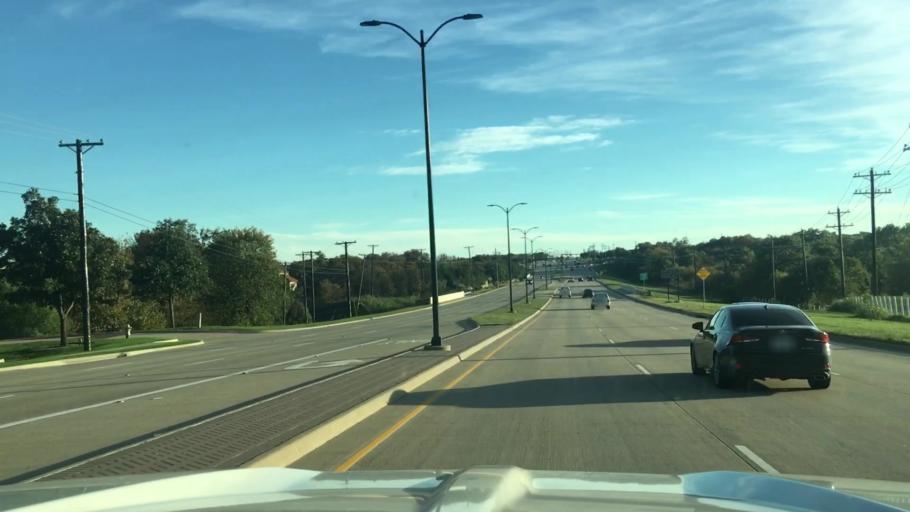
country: US
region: Texas
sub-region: Collin County
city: Frisco
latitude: 33.1803
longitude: -96.8030
